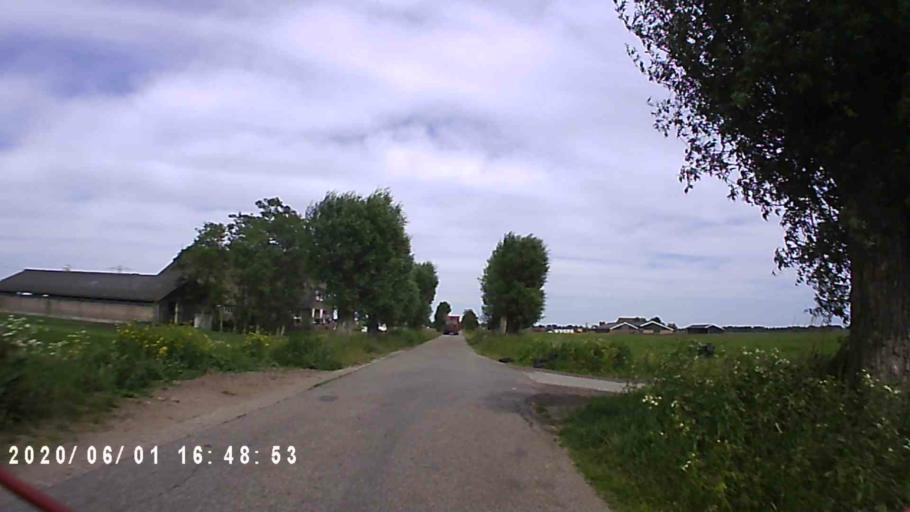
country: NL
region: Friesland
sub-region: Gemeente Tytsjerksteradiel
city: Tytsjerk
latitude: 53.1871
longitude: 5.9034
